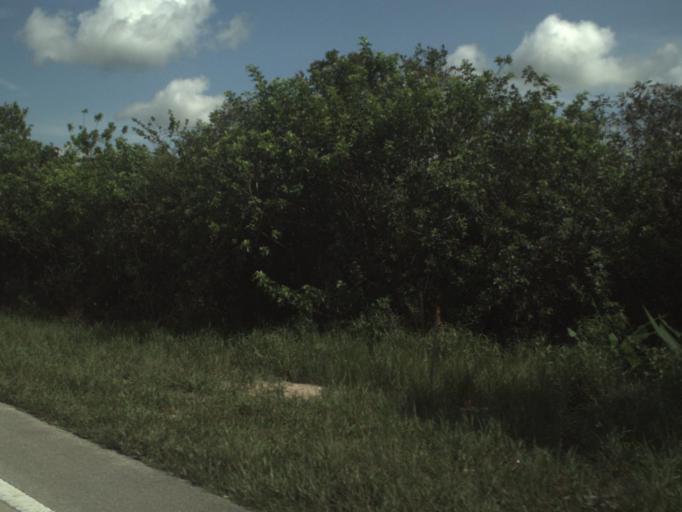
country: US
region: Florida
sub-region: Martin County
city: Indiantown
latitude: 26.9599
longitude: -80.3768
